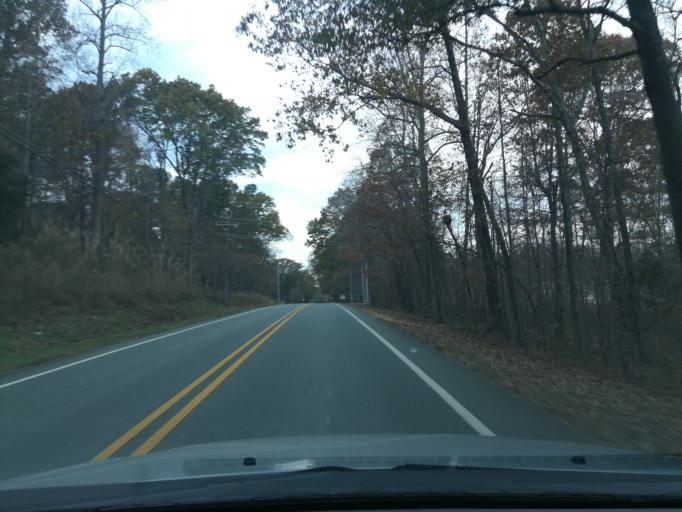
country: US
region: North Carolina
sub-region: Orange County
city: Hillsborough
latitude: 36.0323
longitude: -79.0278
